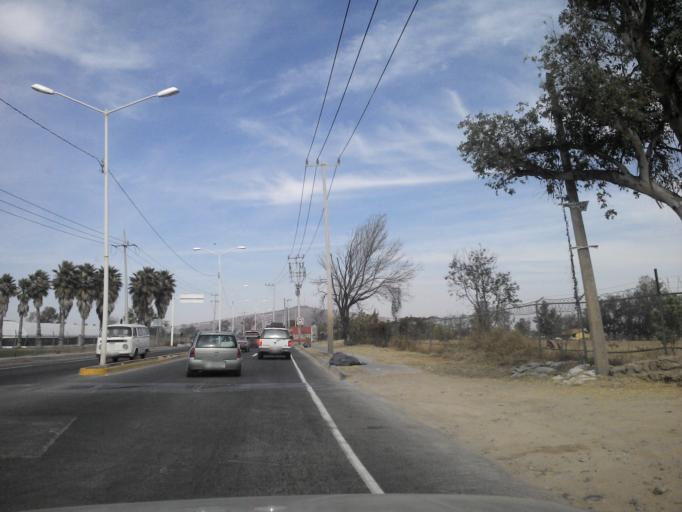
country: MX
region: Jalisco
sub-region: San Pedro Tlaquepaque
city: Paseo del Prado
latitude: 20.5532
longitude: -103.3977
